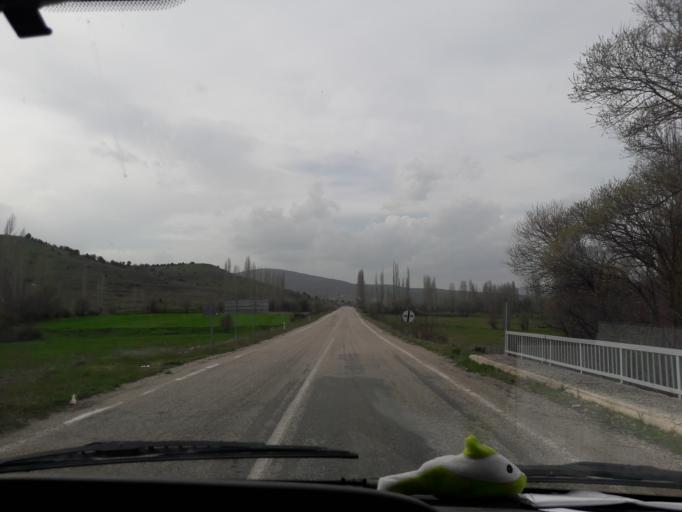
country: TR
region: Gumushane
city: Siran
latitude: 40.1649
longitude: 39.0072
